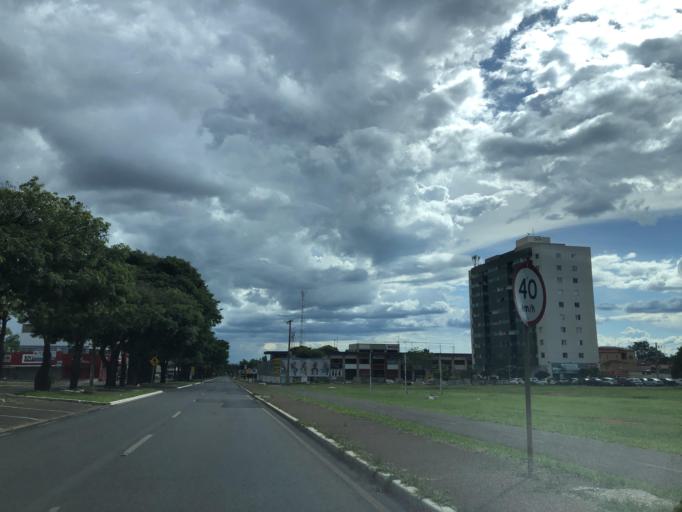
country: BR
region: Goias
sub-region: Luziania
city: Luziania
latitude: -16.0166
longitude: -48.0661
